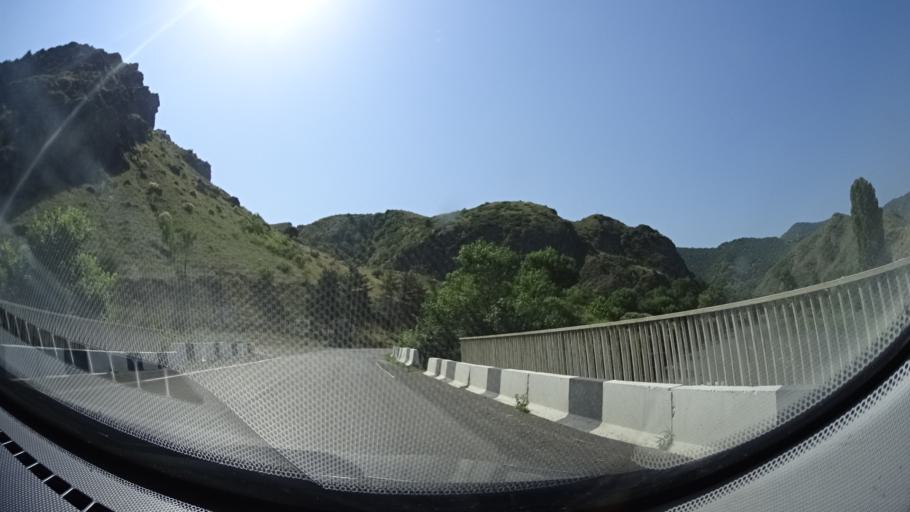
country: GE
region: Samtskhe-Javakheti
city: Akhaltsikhe
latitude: 41.6276
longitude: 43.0509
